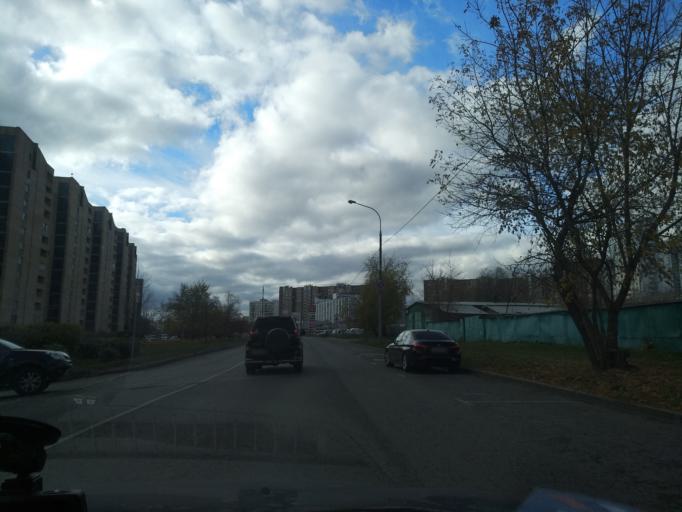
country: RU
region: Moscow
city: Otradnoye
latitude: 55.8726
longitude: 37.5978
